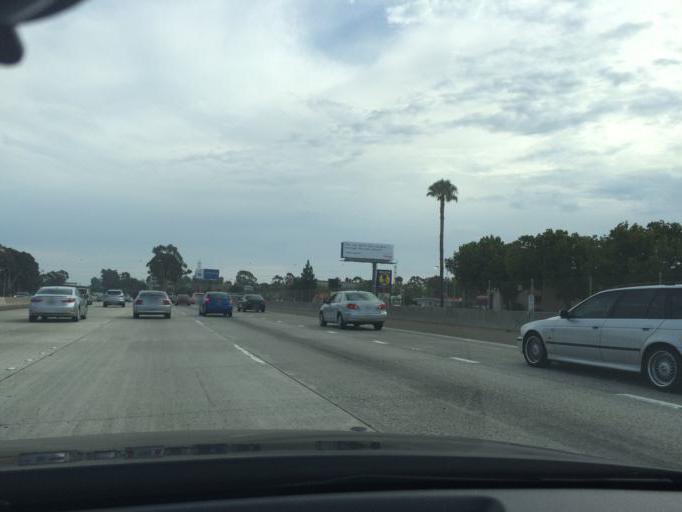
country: US
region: California
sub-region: San Diego County
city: San Diego
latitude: 32.8156
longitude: -117.1503
